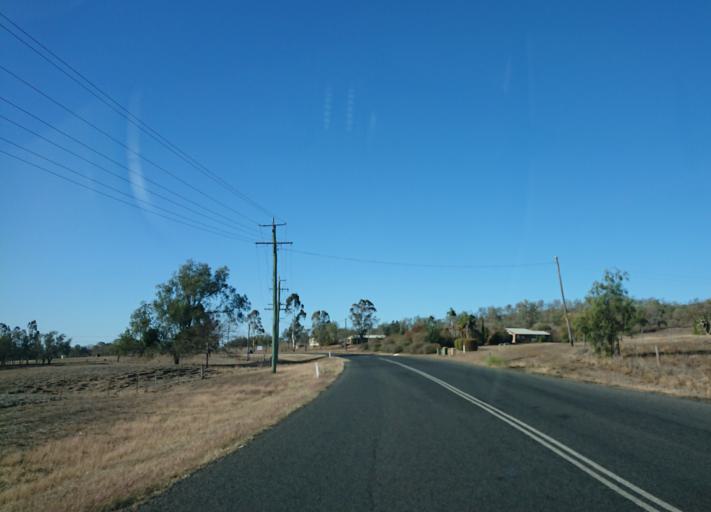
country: AU
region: Queensland
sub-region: Lockyer Valley
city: Gatton
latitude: -27.6449
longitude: 152.1819
